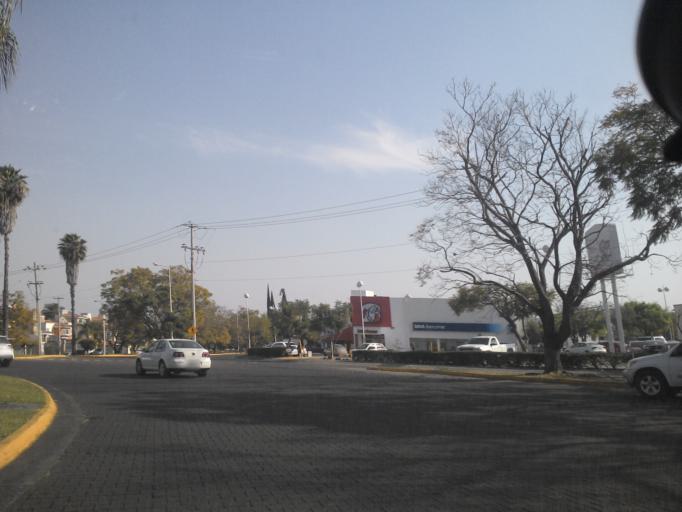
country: MX
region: Jalisco
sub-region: Tlajomulco de Zuniga
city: Palomar
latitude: 20.6018
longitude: -103.4473
